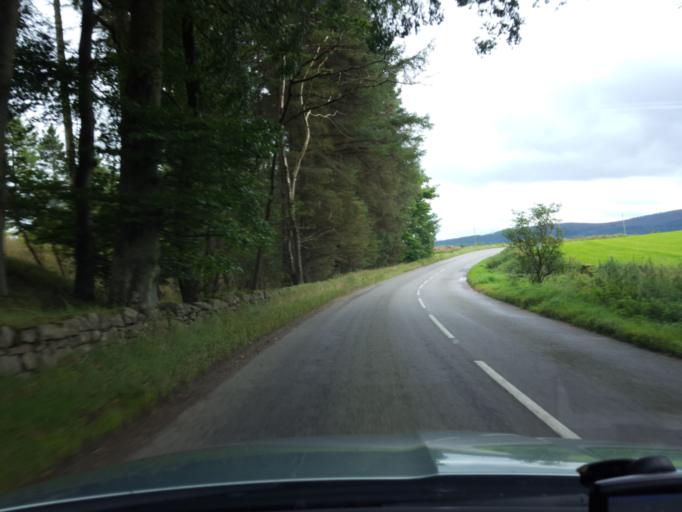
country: GB
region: Scotland
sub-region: Aberdeenshire
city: Kemnay
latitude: 57.1558
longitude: -2.4302
